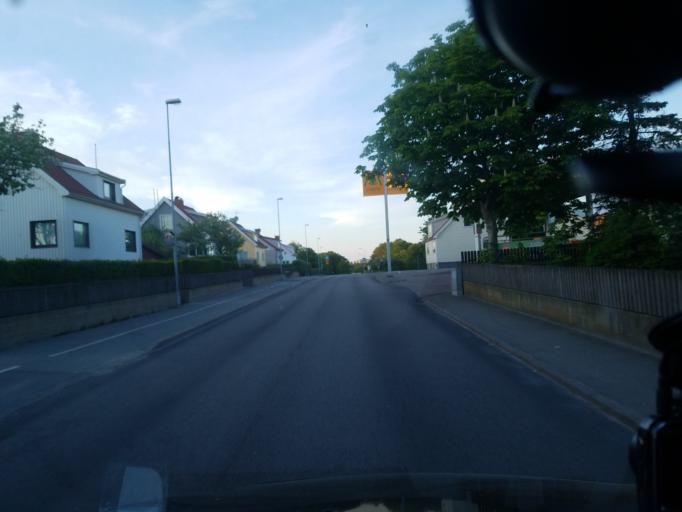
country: SE
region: Vaestra Goetaland
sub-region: Lysekils Kommun
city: Lysekil
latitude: 58.2801
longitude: 11.4564
